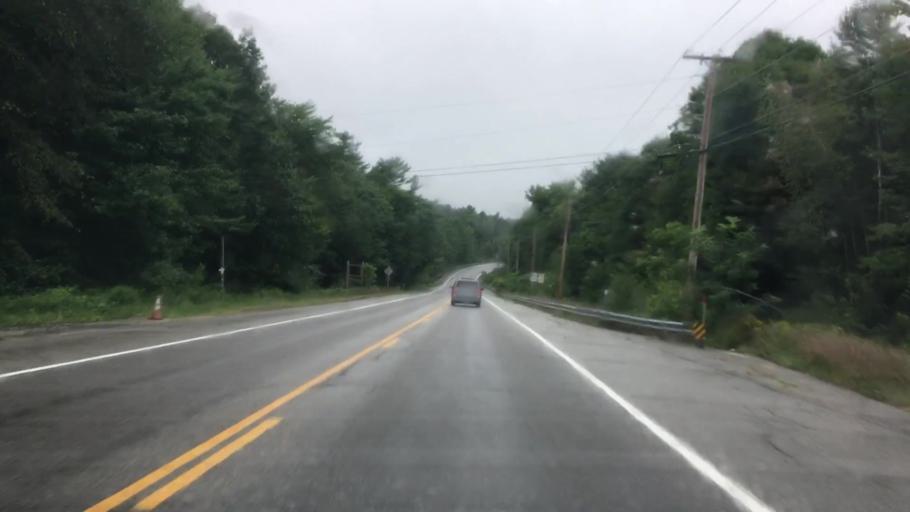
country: US
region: Maine
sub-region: Cumberland County
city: Raymond
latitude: 43.9578
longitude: -70.5635
